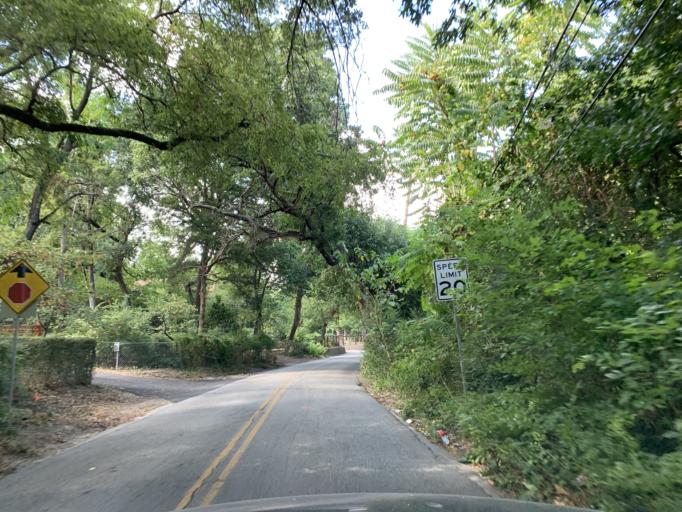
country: US
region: Texas
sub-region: Dallas County
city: Cockrell Hill
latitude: 32.7428
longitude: -96.8702
